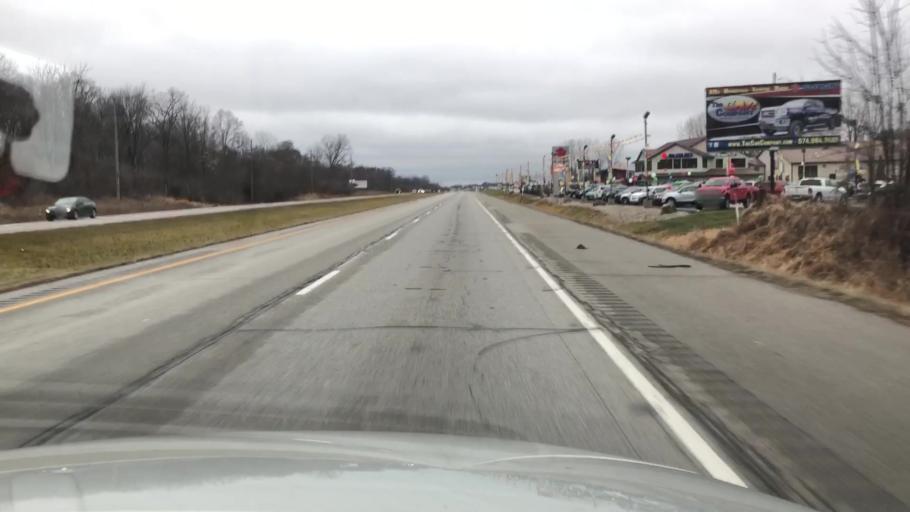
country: US
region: Indiana
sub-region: Kosciusko County
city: Winona Lake
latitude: 41.2172
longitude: -85.7651
